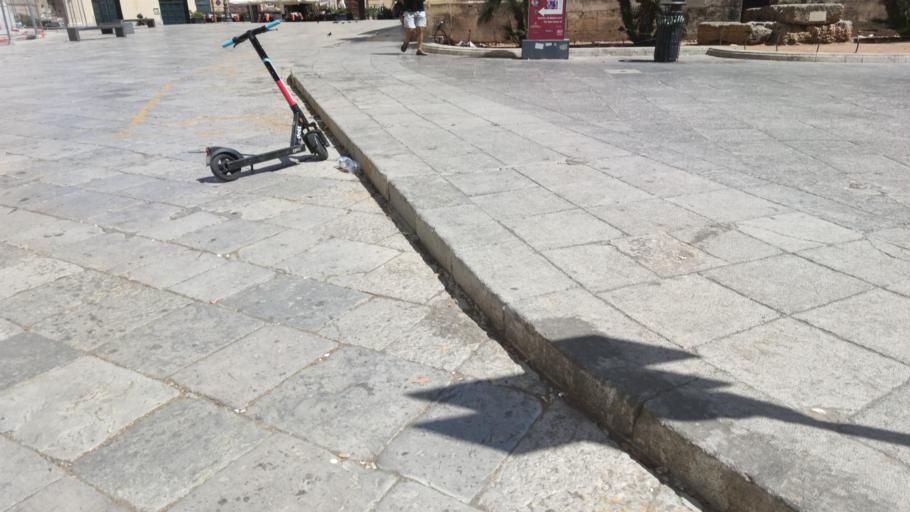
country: IT
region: Sicily
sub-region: Palermo
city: Palermo
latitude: 38.1148
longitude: 13.3621
